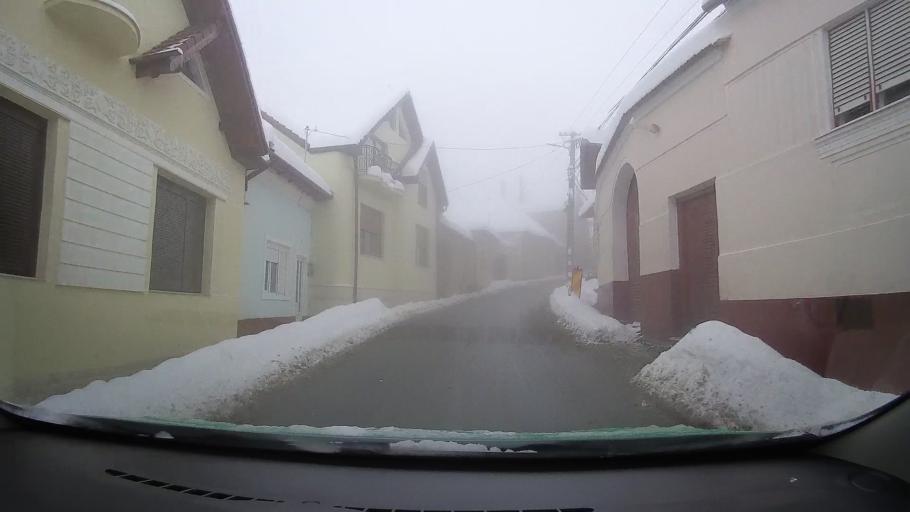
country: RO
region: Sibiu
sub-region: Comuna Poiana Sibiului
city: Poiana Sibiului
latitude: 45.8084
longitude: 23.7337
